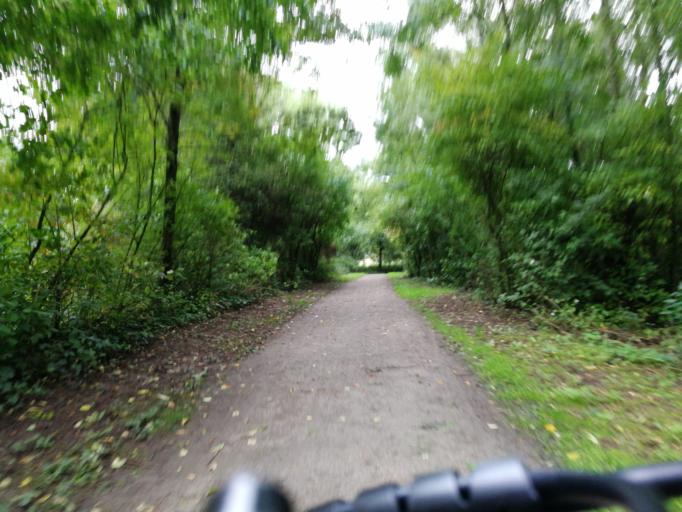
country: DE
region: North Rhine-Westphalia
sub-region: Regierungsbezirk Dusseldorf
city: Neuss
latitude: 51.1483
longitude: 6.7329
